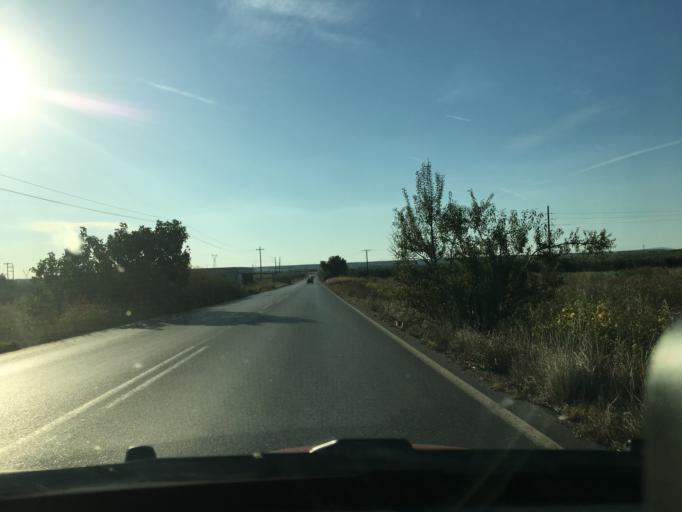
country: GR
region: Central Macedonia
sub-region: Nomos Chalkidikis
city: Kalyves Polygyrou
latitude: 40.2837
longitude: 23.3747
